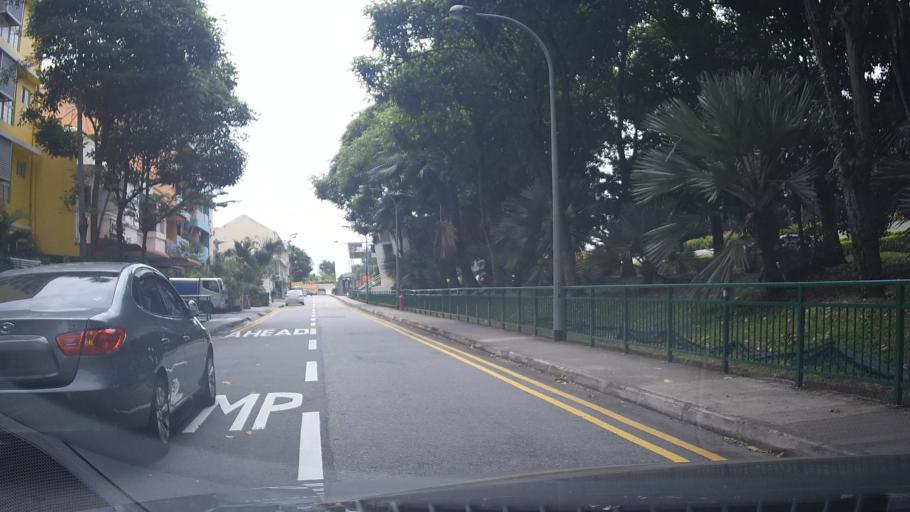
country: SG
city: Singapore
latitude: 1.3111
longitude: 103.8759
